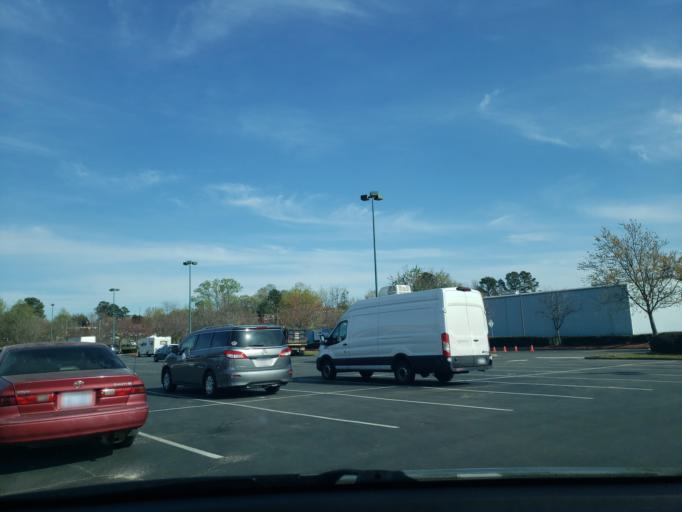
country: US
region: North Carolina
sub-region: Durham County
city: Durham
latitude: 36.0289
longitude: -78.9192
